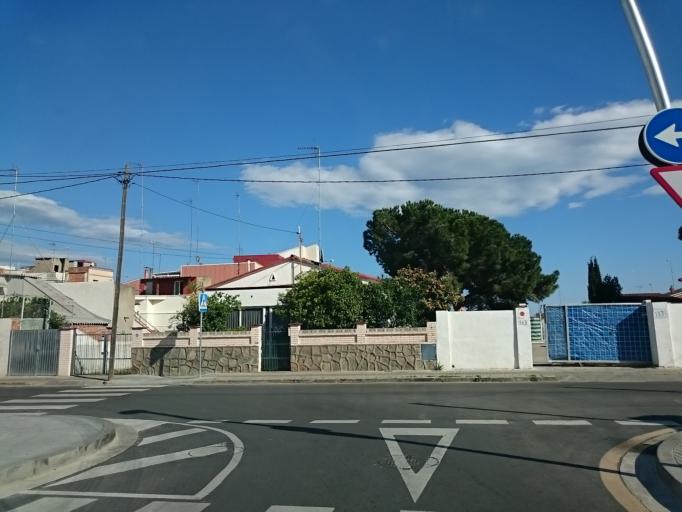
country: ES
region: Catalonia
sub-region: Provincia de Barcelona
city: Viladecans
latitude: 41.3157
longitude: 2.0062
